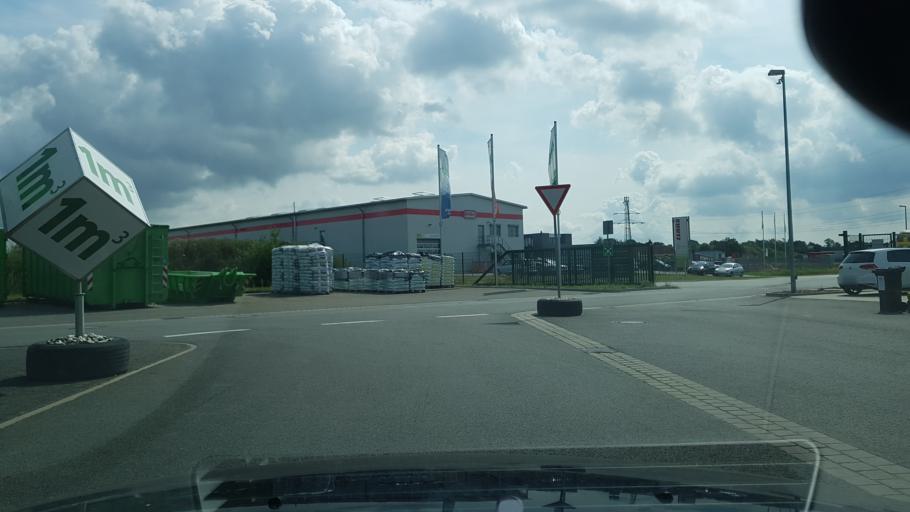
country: DE
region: Lower Saxony
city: Sulingen
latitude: 52.6737
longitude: 8.8034
